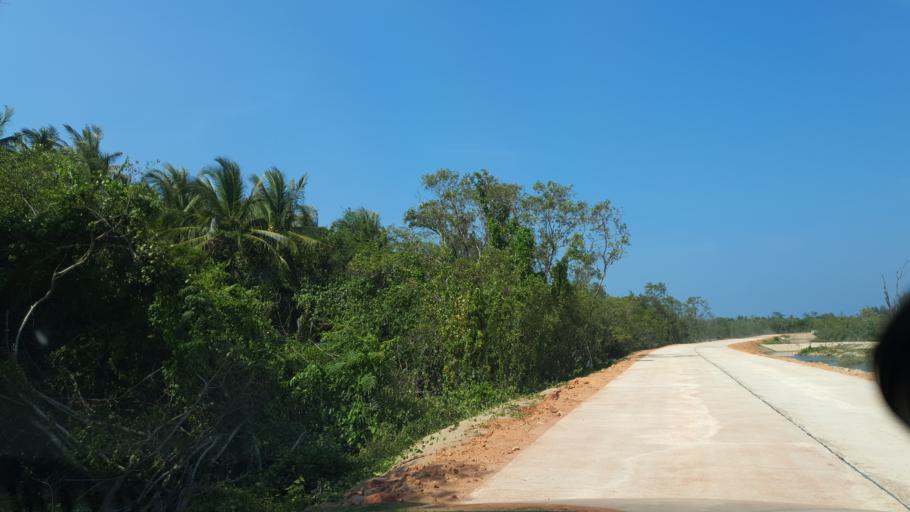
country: TH
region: Surat Thani
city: Tha Chana
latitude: 9.5911
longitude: 99.2076
